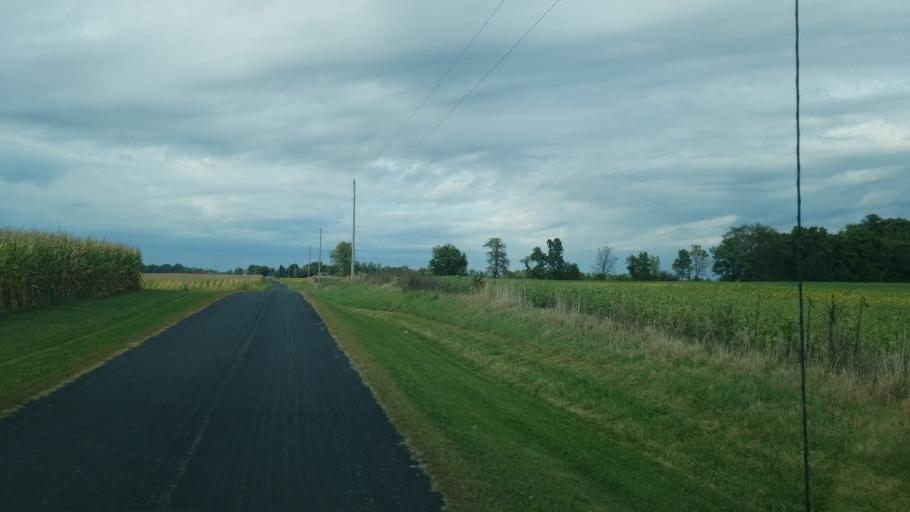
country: US
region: Ohio
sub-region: Wyandot County
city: Upper Sandusky
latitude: 40.9115
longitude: -83.1505
